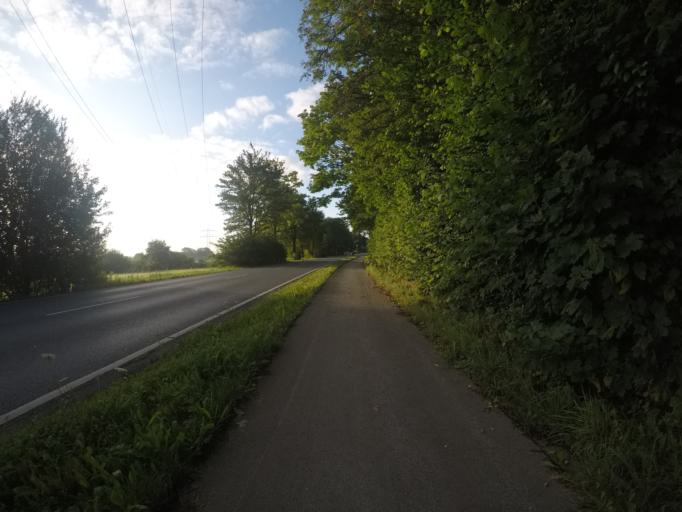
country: DE
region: North Rhine-Westphalia
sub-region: Regierungsbezirk Detmold
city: Hiddenhausen
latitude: 52.1398
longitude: 8.6218
